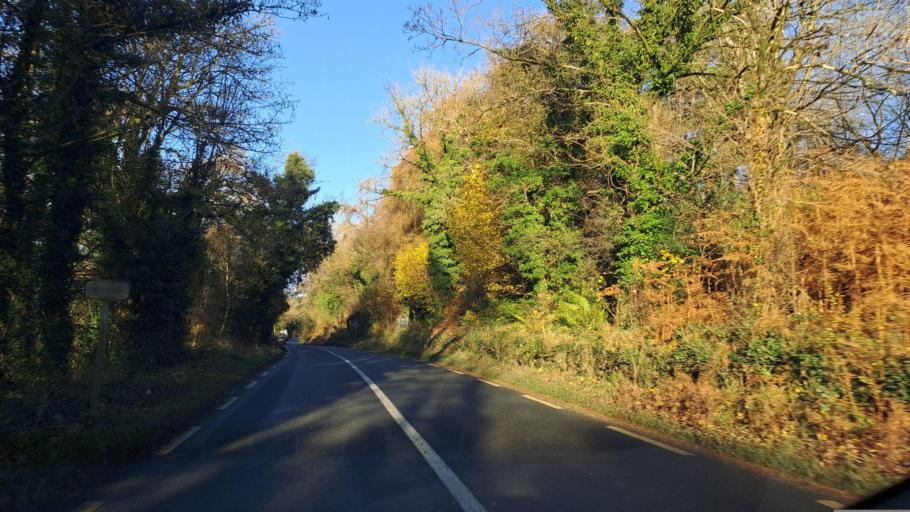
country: IE
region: Ulster
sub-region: An Cabhan
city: Mullagh
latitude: 53.8569
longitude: -6.9548
